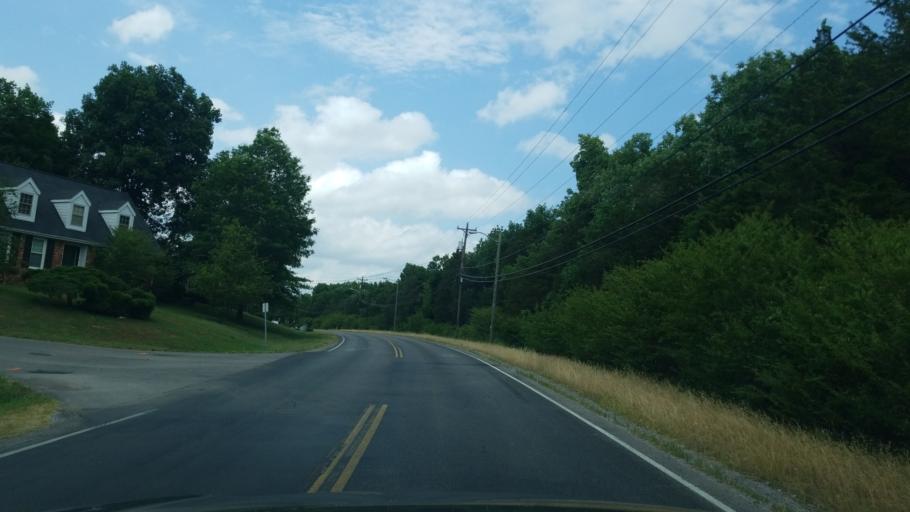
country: US
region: Tennessee
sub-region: Rutherford County
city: La Vergne
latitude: 36.0978
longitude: -86.6031
